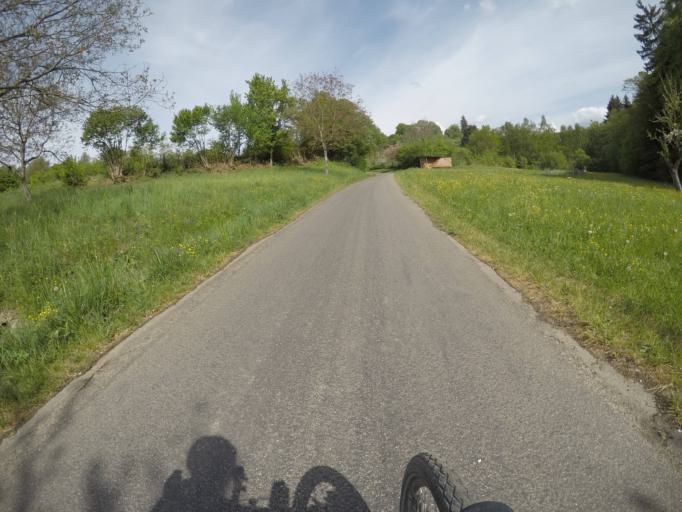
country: DE
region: Baden-Wuerttemberg
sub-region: Tuebingen Region
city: Tuebingen
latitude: 48.5408
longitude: 9.0193
